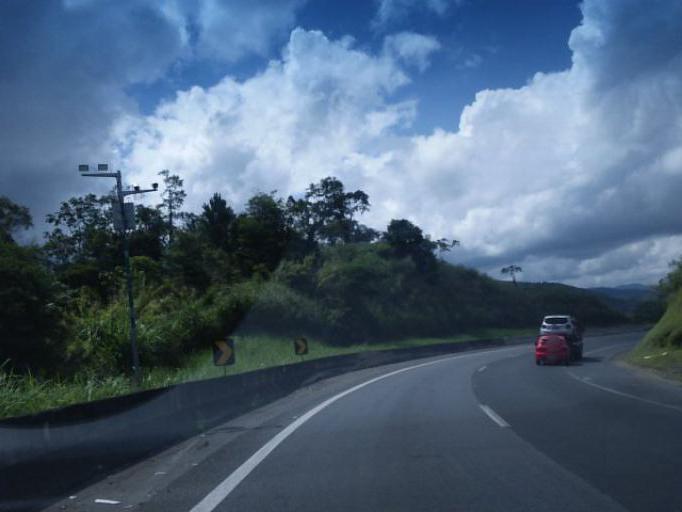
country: BR
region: Sao Paulo
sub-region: Cajati
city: Cajati
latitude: -24.8574
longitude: -48.2123
